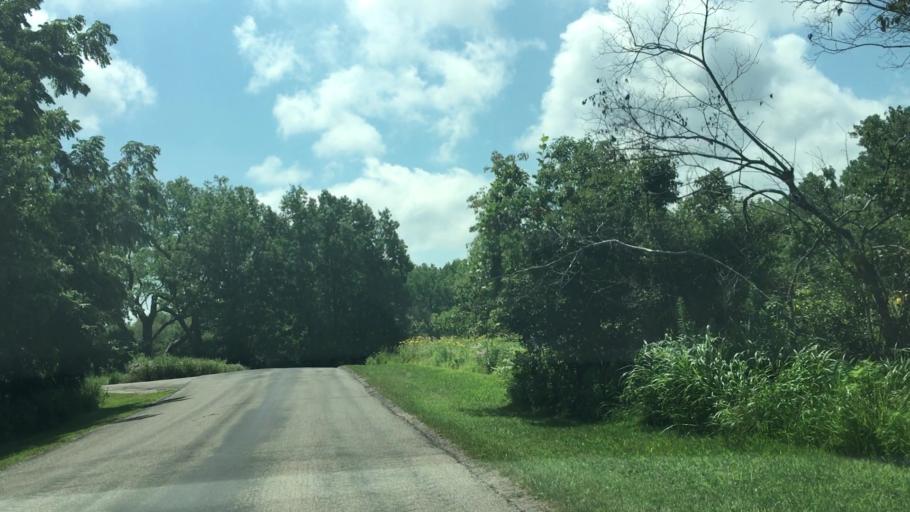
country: US
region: Iowa
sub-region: Johnson County
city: Tiffin
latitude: 41.7345
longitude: -91.7245
